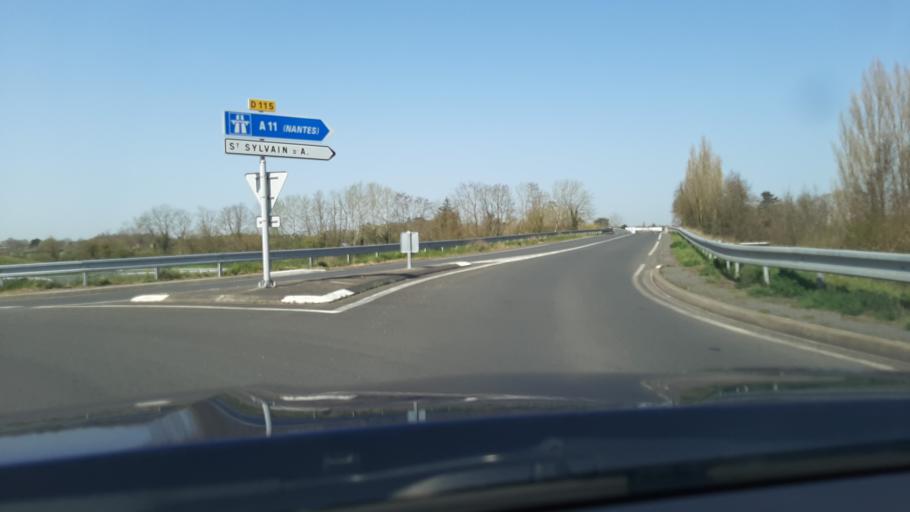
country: FR
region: Pays de la Loire
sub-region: Departement de Maine-et-Loire
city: Pellouailles-les-Vignes
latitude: 47.5081
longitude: -0.4460
